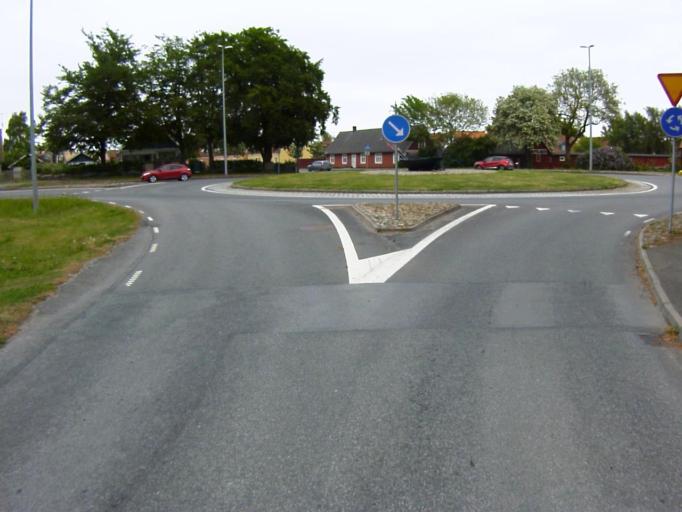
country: SE
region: Skane
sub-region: Kristianstads Kommun
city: Ahus
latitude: 55.9233
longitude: 14.2881
